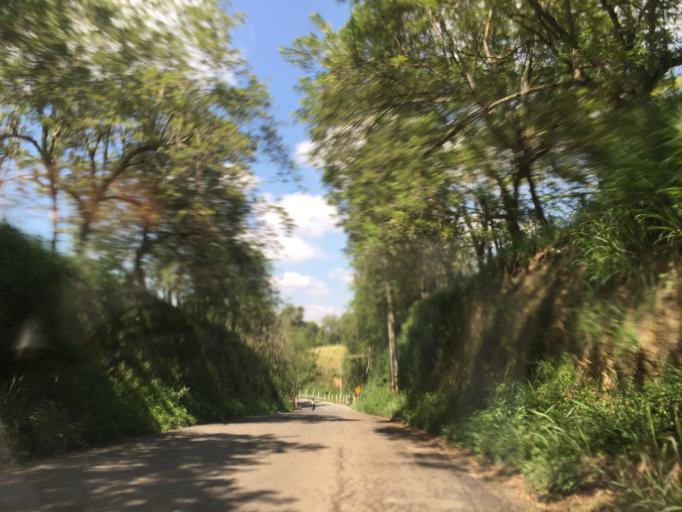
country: CO
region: Valle del Cauca
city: Alcala
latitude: 4.7231
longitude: -75.7929
